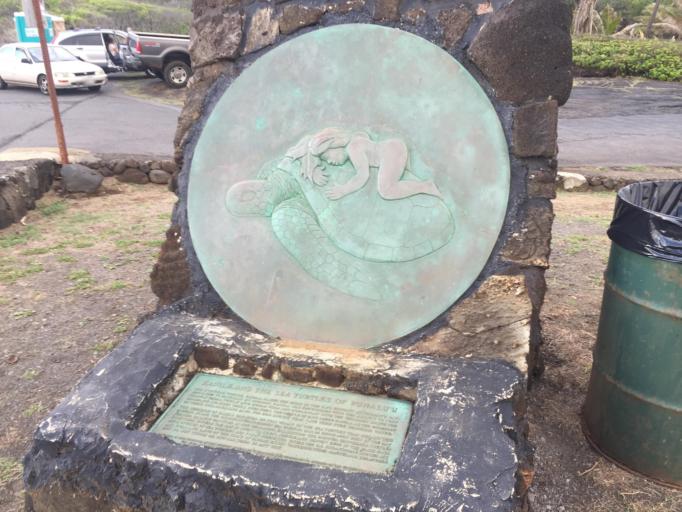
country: US
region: Hawaii
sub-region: Hawaii County
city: Pahala
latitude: 19.1341
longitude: -155.5055
